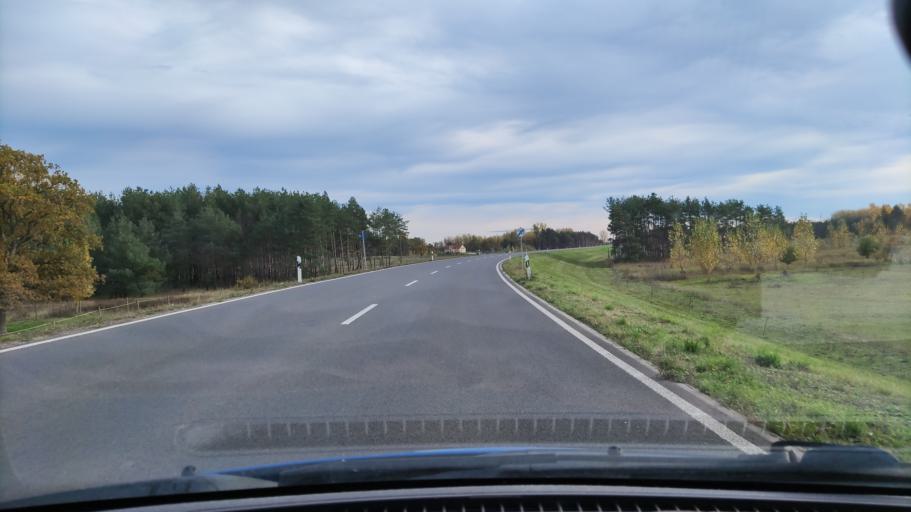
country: DE
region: Brandenburg
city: Breese
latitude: 53.0065
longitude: 11.7773
